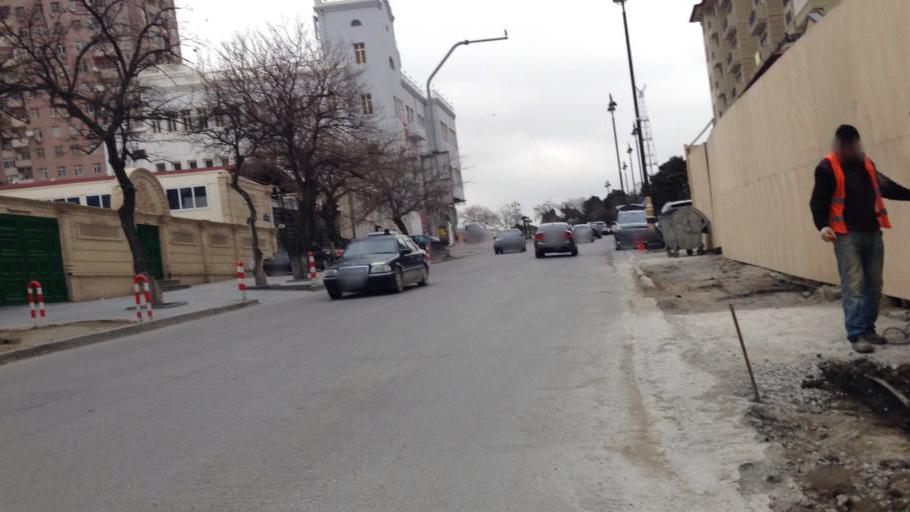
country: AZ
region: Baki
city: Baku
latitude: 40.3902
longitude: 49.8497
